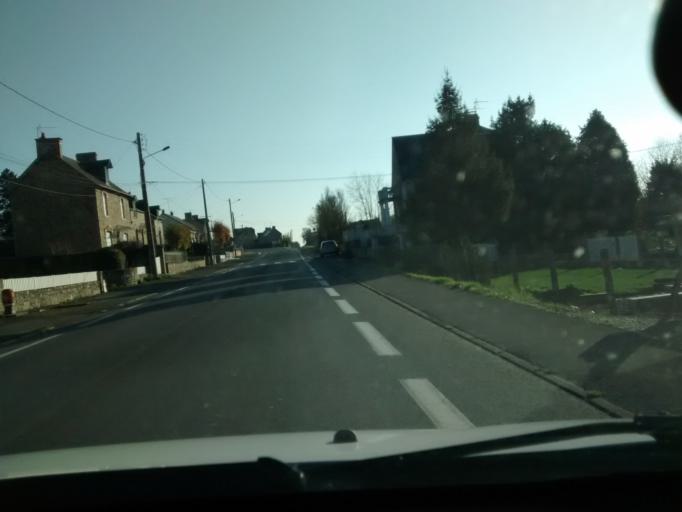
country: FR
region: Lower Normandy
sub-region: Departement de la Manche
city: Pontorson
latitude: 48.5481
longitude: -1.5030
